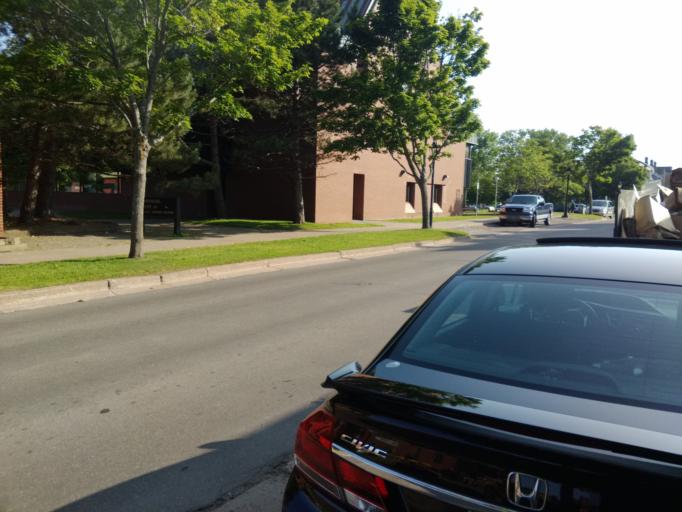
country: CA
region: Prince Edward Island
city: Charlottetown
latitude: 46.2315
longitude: -63.1255
